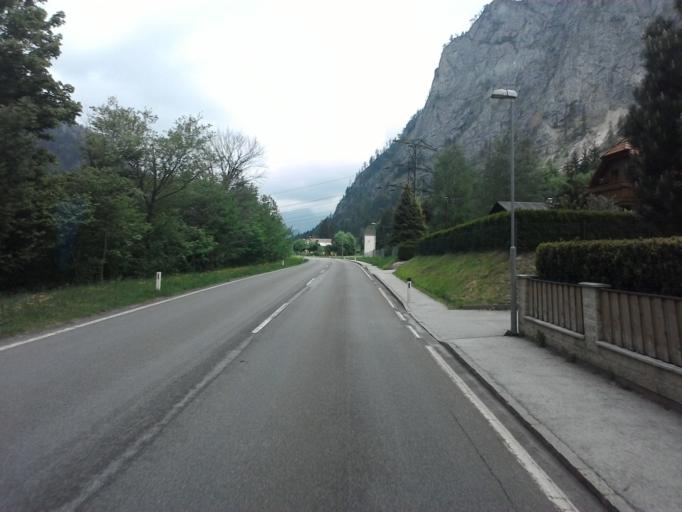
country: AT
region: Styria
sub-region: Politischer Bezirk Leoben
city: Hieflau
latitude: 47.6189
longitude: 14.7512
